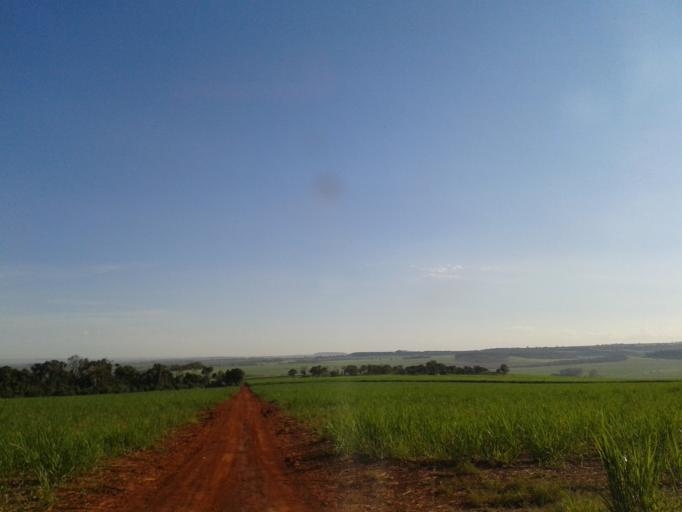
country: BR
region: Minas Gerais
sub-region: Centralina
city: Centralina
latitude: -18.6659
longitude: -49.2592
